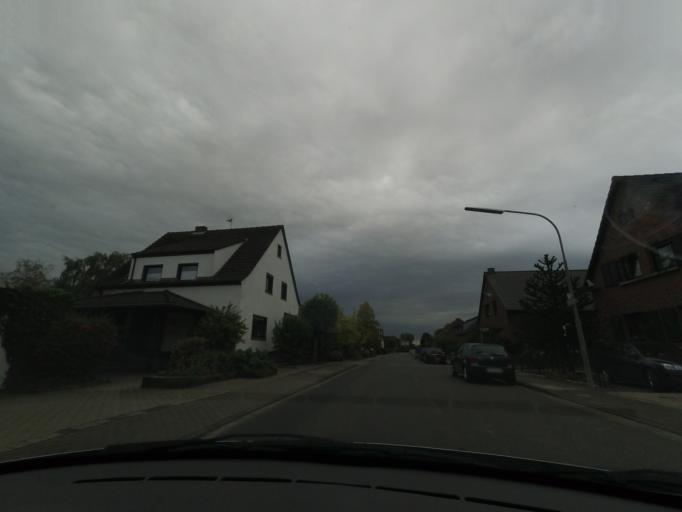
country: DE
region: North Rhine-Westphalia
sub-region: Regierungsbezirk Dusseldorf
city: Korschenbroich
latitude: 51.1859
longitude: 6.5591
